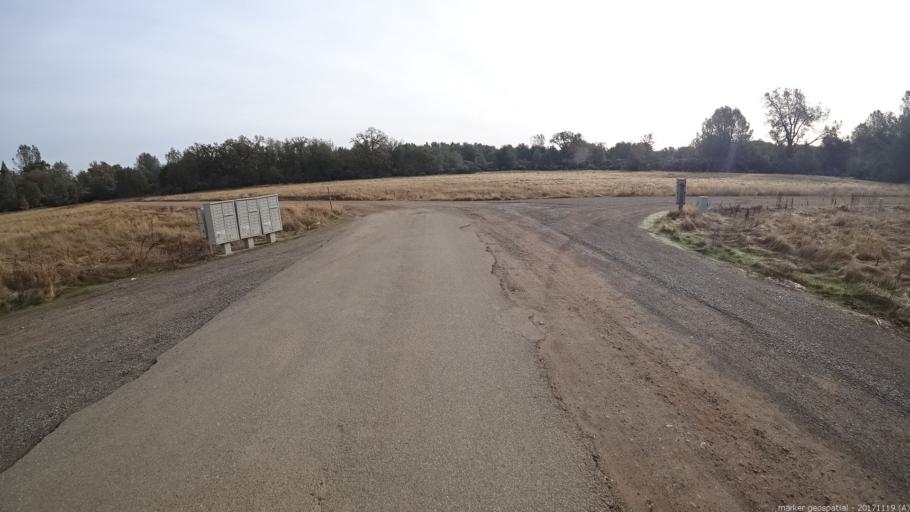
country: US
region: California
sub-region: Shasta County
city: Anderson
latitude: 40.5184
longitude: -122.3053
